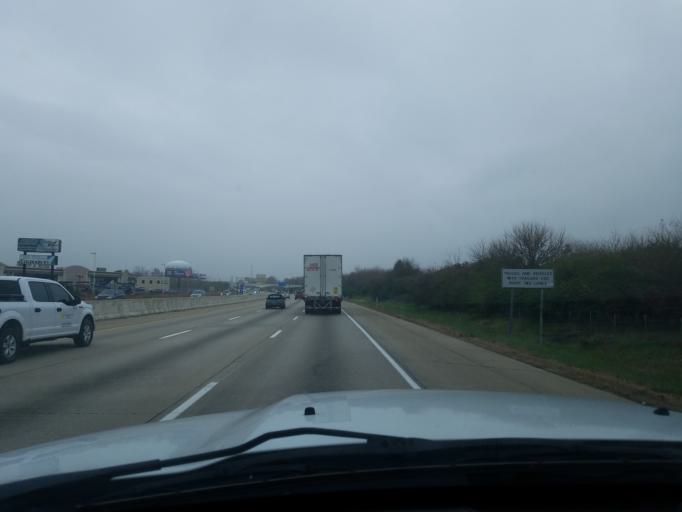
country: US
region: Indiana
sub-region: Marion County
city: Beech Grove
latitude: 39.7050
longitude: -86.0683
